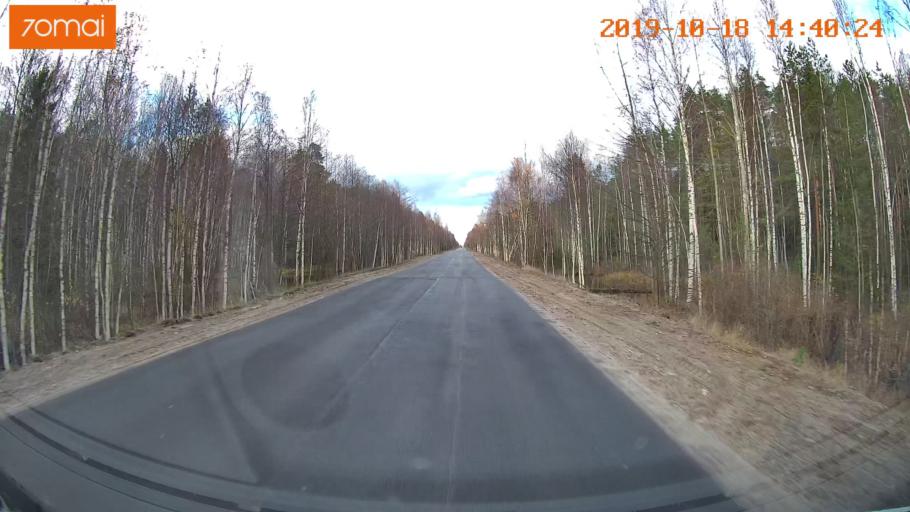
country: RU
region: Vladimir
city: Velikodvorskiy
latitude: 55.2760
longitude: 40.6689
